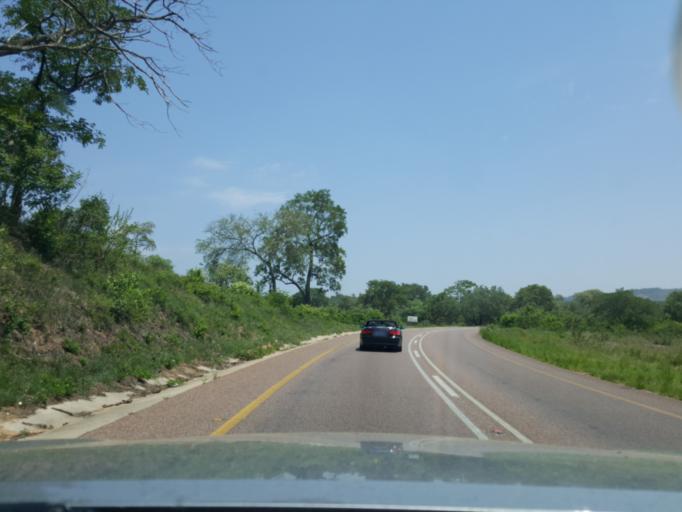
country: ZA
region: Mpumalanga
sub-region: Ehlanzeni District
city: Graksop
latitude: -25.0132
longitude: 31.1138
